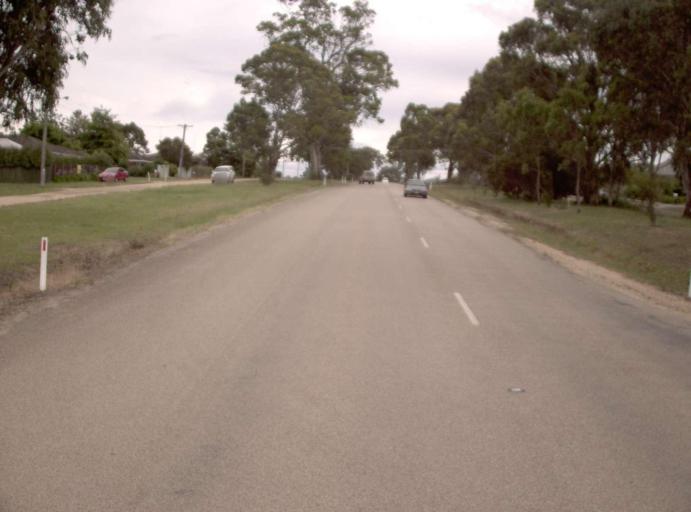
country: AU
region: Victoria
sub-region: East Gippsland
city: Bairnsdale
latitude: -37.8044
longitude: 147.6164
